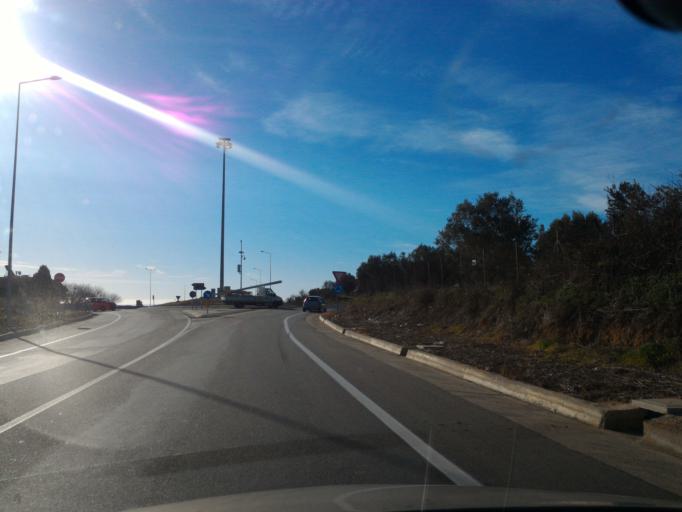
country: IT
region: Calabria
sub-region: Provincia di Crotone
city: Isola di Capo Rizzuto
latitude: 38.9512
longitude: 17.0826
